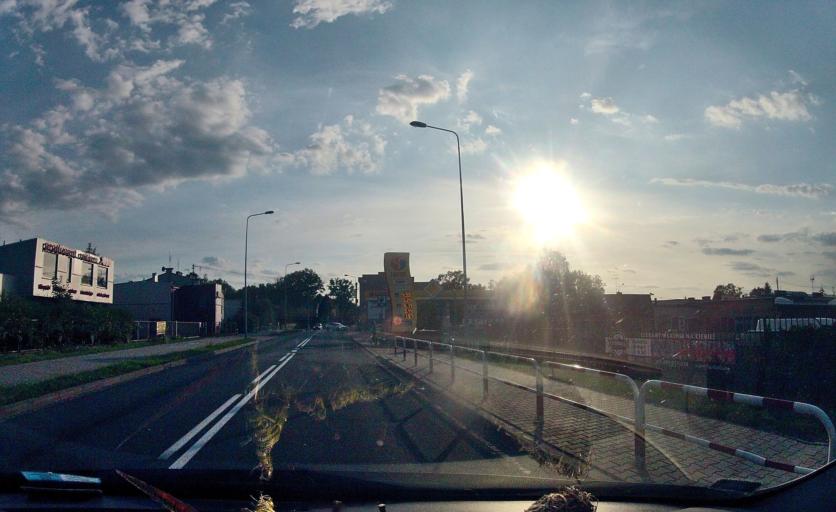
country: PL
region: Opole Voivodeship
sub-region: Powiat kluczborski
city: Kluczbork
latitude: 50.9739
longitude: 18.2256
